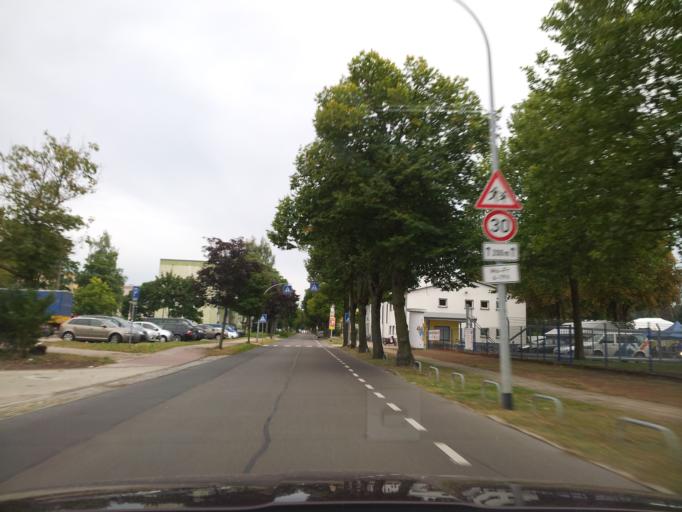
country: DE
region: Brandenburg
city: Luckenwalde
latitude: 52.1035
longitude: 13.1495
